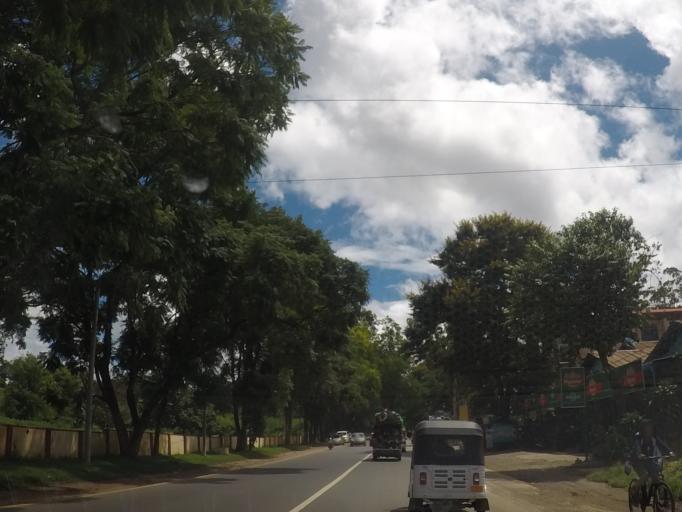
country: MM
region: Mandalay
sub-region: Pyin Oo Lwin District
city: Pyin Oo Lwin
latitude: 22.0395
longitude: 96.4935
